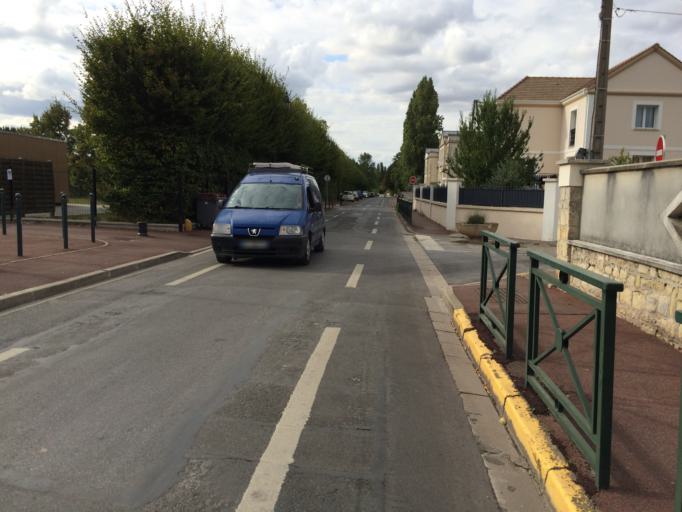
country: FR
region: Ile-de-France
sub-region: Departement de l'Essonne
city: Soisy-sur-Seine
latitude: 48.6488
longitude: 2.4427
